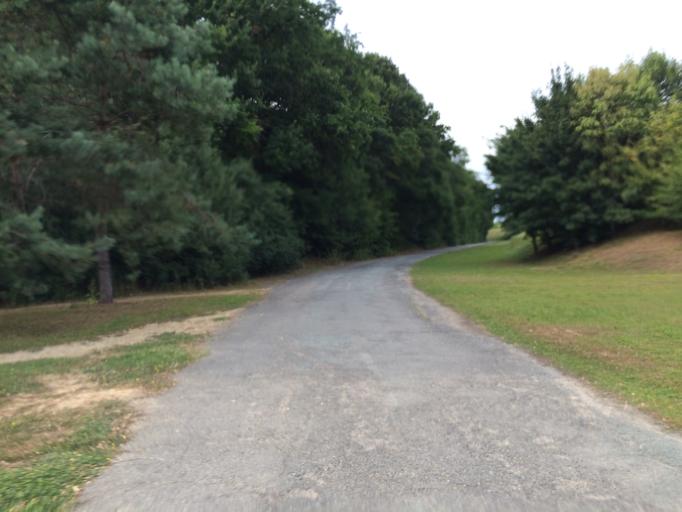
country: FR
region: Ile-de-France
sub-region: Departement de Seine-et-Marne
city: Lieusaint
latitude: 48.6560
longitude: 2.5476
